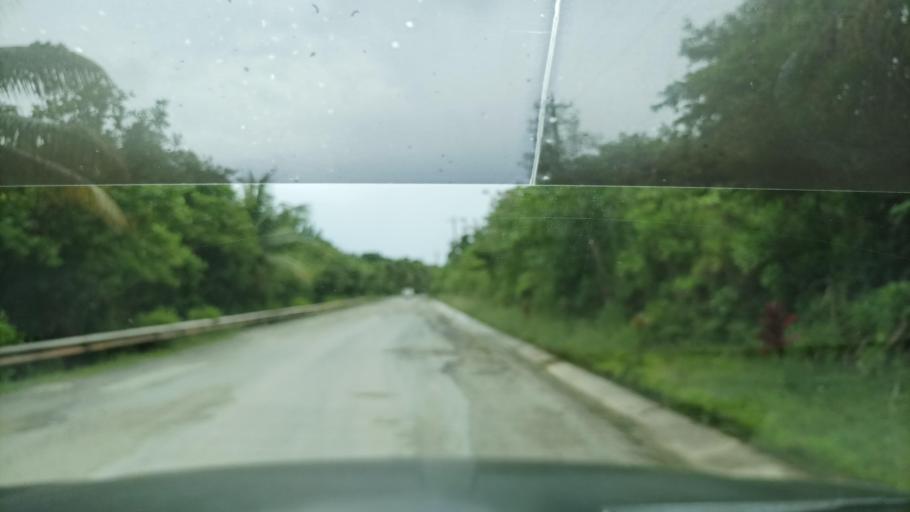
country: FM
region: Yap
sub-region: Weloy Municipality
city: Colonia
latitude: 9.5522
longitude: 138.1468
